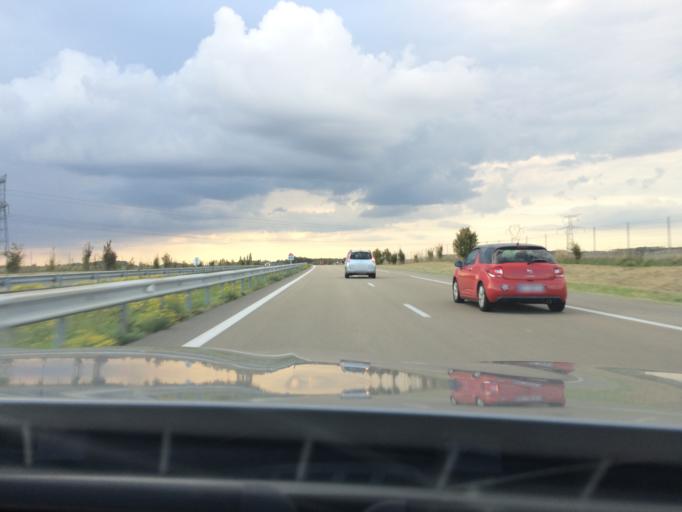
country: FR
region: Ile-de-France
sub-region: Departement de Seine-et-Marne
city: Egreville
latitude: 48.1754
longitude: 2.8545
